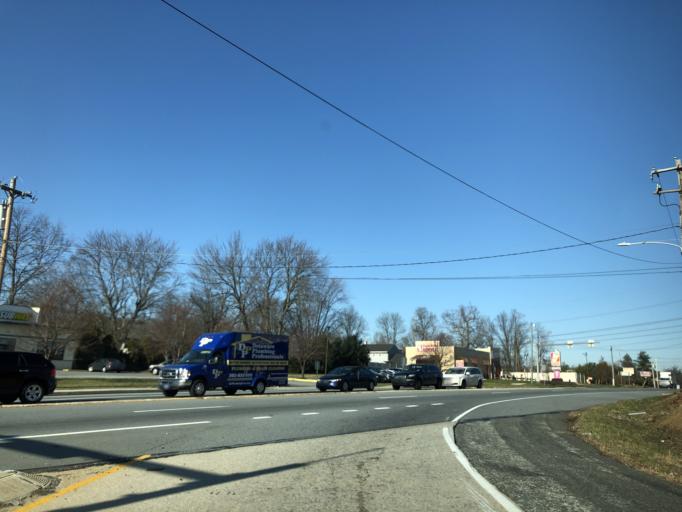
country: US
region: Pennsylvania
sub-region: Delaware County
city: Linwood
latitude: 39.8351
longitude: -75.4242
